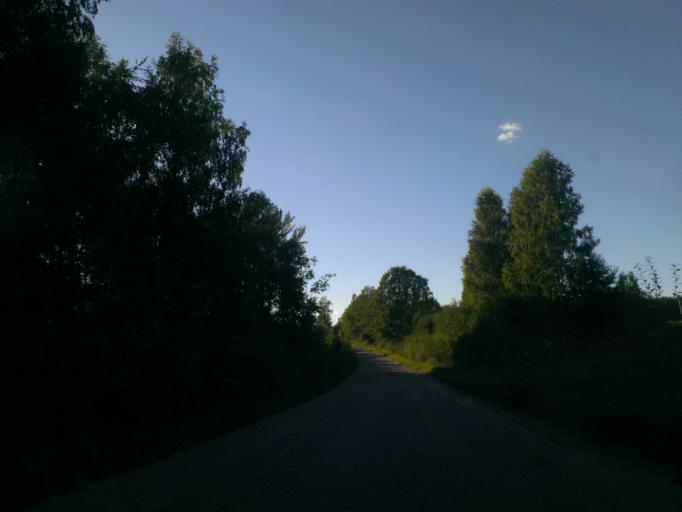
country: LV
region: Malpils
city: Malpils
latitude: 57.0847
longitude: 25.0557
